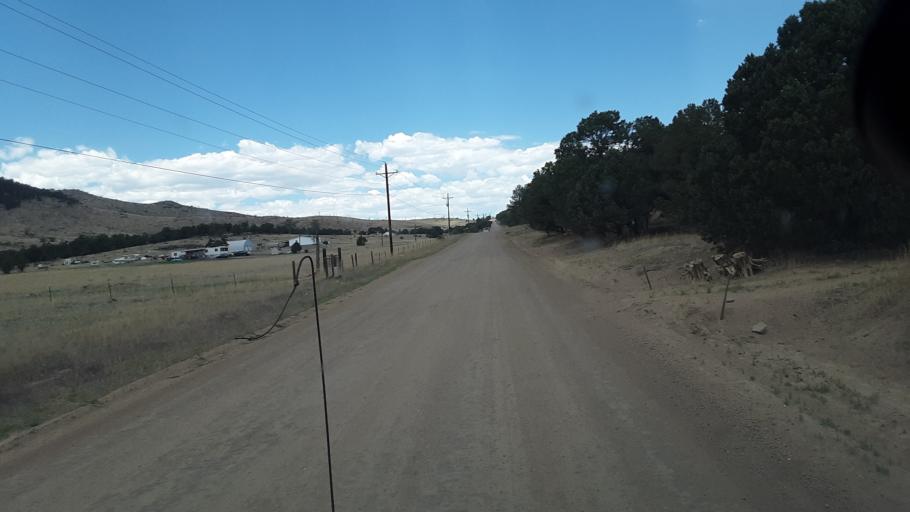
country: US
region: Colorado
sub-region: Custer County
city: Westcliffe
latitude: 38.3144
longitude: -105.4867
